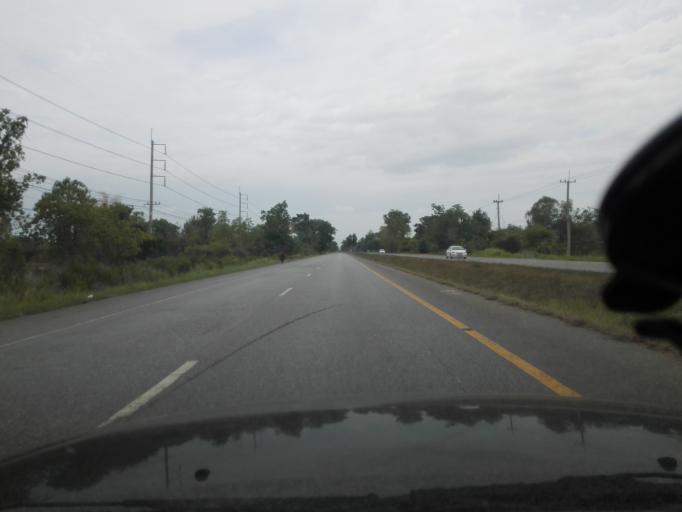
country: TH
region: Kamphaeng Phet
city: Khlong Khlung
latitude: 16.1130
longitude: 99.7192
